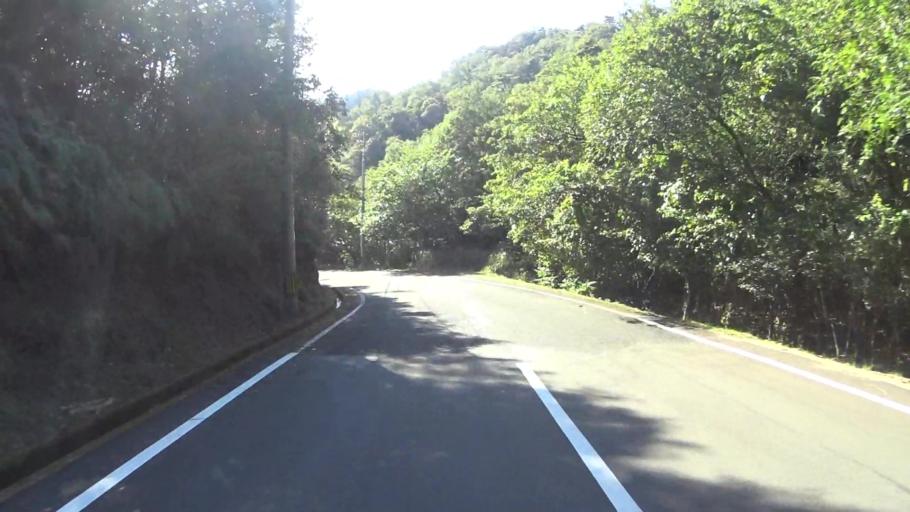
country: JP
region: Hyogo
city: Toyooka
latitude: 35.6426
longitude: 134.8884
